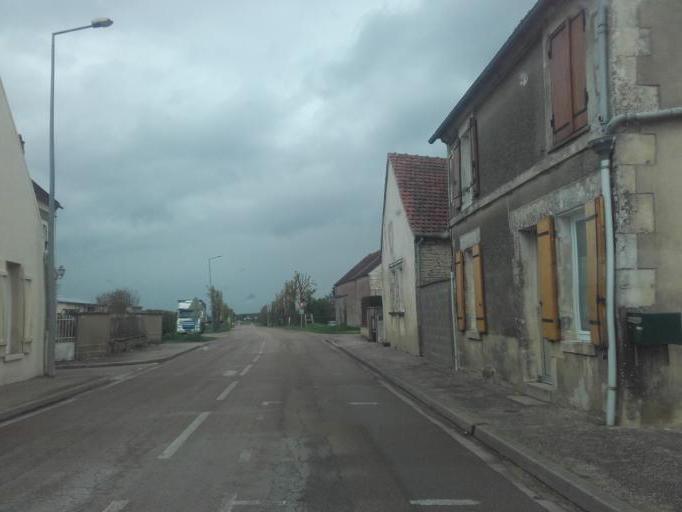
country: FR
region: Bourgogne
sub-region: Departement de l'Yonne
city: Chablis
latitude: 47.7286
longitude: 3.8529
